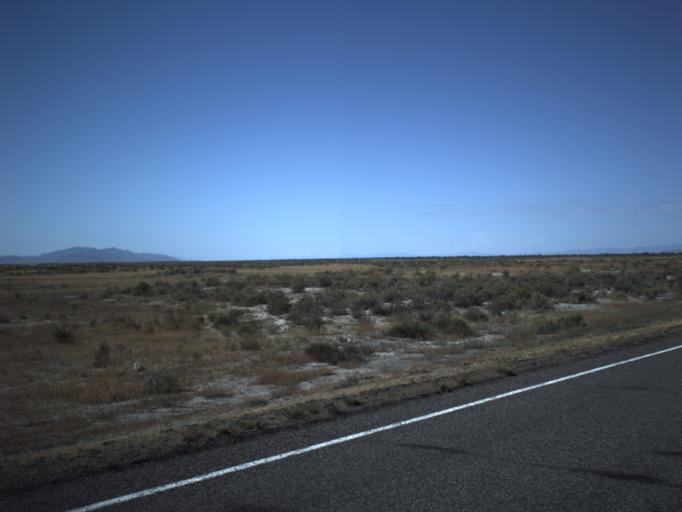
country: US
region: Utah
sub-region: Millard County
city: Delta
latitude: 39.3098
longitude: -112.7782
